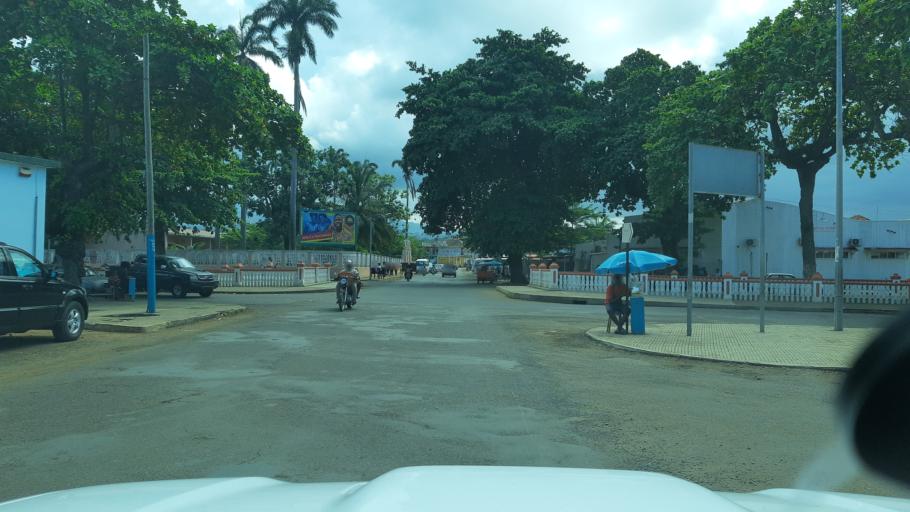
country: ST
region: Sao Tome Island
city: Sao Tome
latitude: 0.3368
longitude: 6.7320
